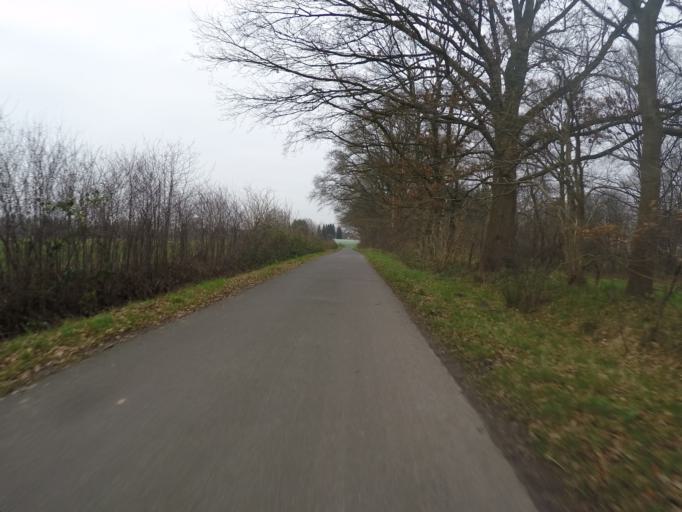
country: DE
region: Schleswig-Holstein
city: Borstel-Hohenraden
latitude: 53.6809
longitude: 9.8180
